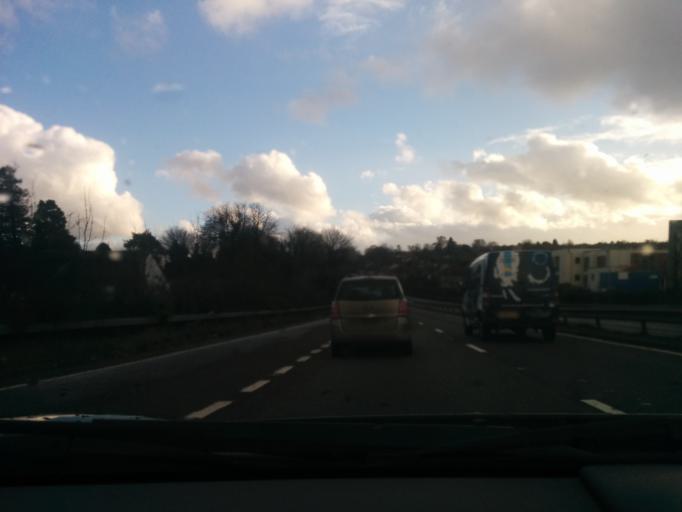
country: GB
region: England
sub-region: Oxfordshire
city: Boars Hill
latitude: 51.7519
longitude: -1.2961
